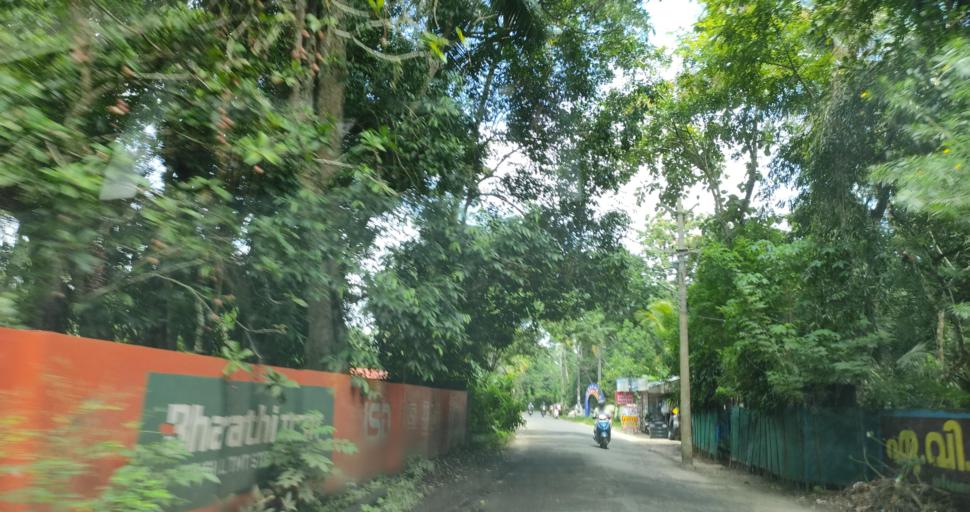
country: IN
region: Kerala
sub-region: Alappuzha
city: Vayalar
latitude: 9.7133
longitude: 76.3372
